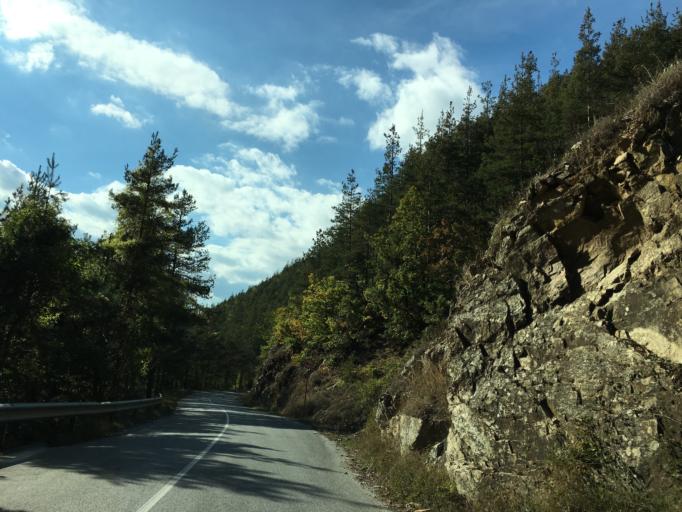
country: BG
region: Smolyan
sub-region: Obshtina Madan
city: Madan
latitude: 41.4573
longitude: 24.9813
